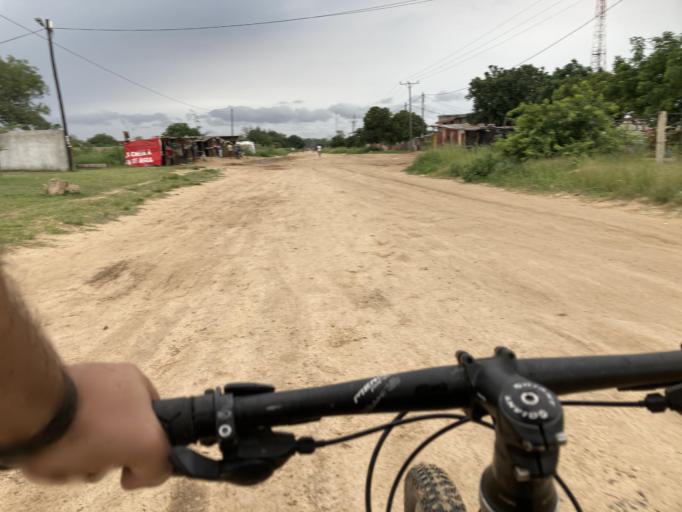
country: MZ
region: Maputo City
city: Maputo
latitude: -26.0418
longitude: 32.5385
